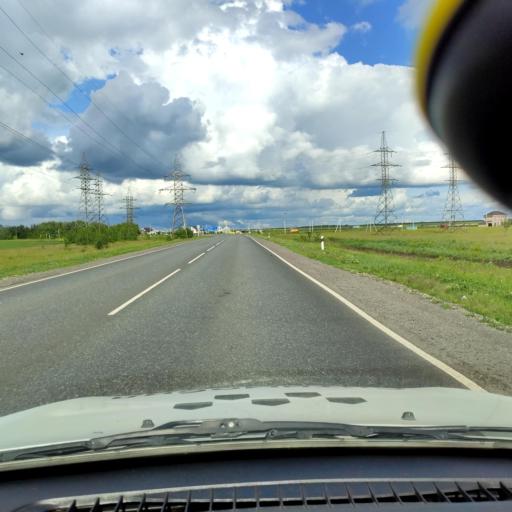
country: RU
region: Samara
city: Povolzhskiy
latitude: 53.6563
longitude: 49.7020
